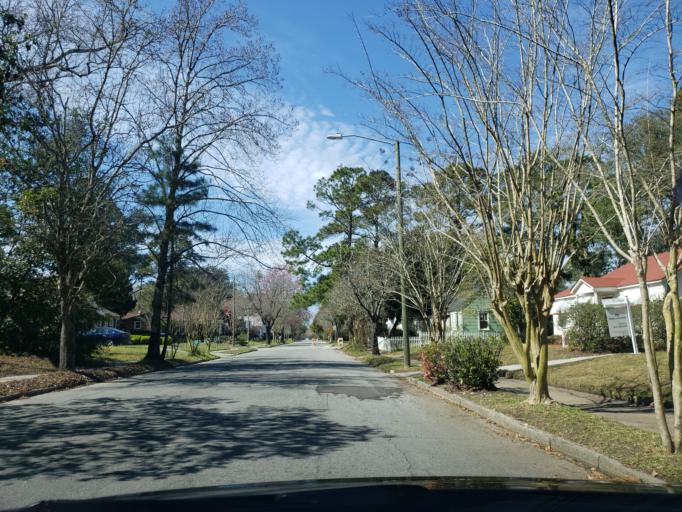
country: US
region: Georgia
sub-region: Chatham County
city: Thunderbolt
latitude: 32.0402
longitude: -81.0835
